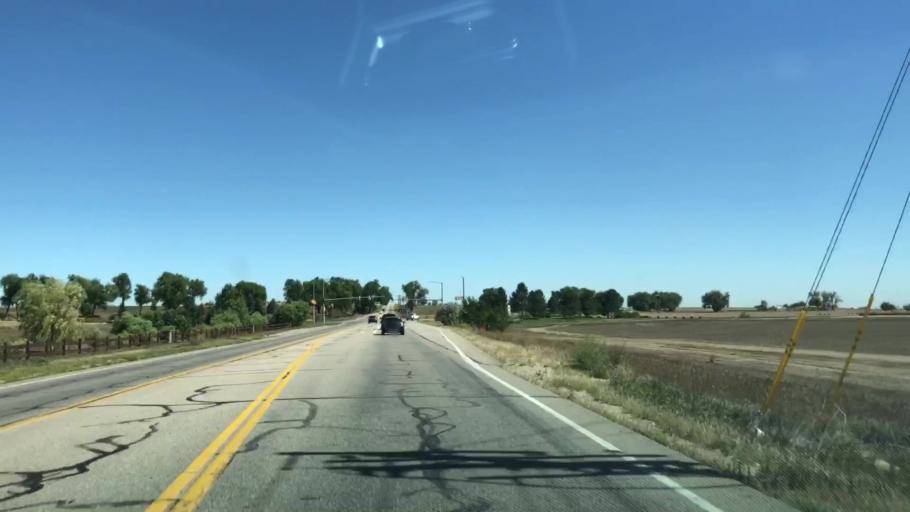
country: US
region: Colorado
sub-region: Weld County
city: Windsor
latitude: 40.5229
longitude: -104.9575
